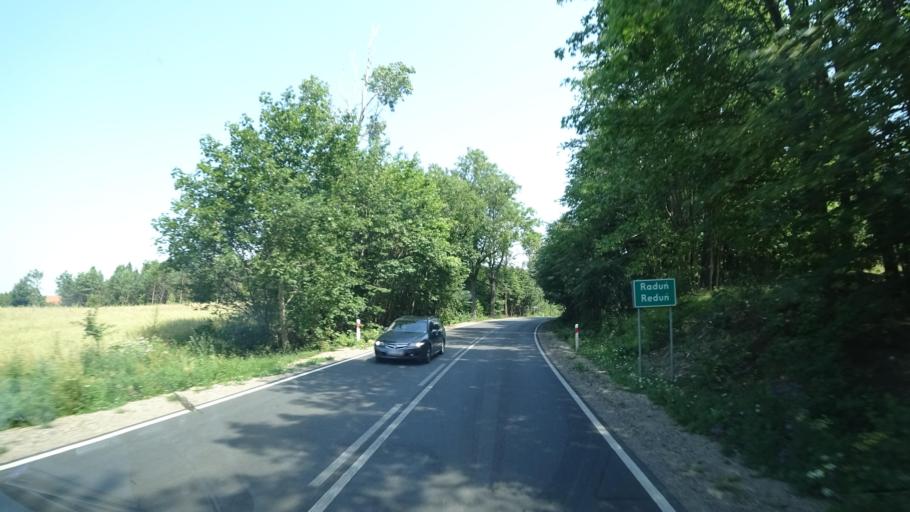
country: PL
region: Pomeranian Voivodeship
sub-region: Powiat koscierski
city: Dziemiany
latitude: 53.9673
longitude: 17.7567
